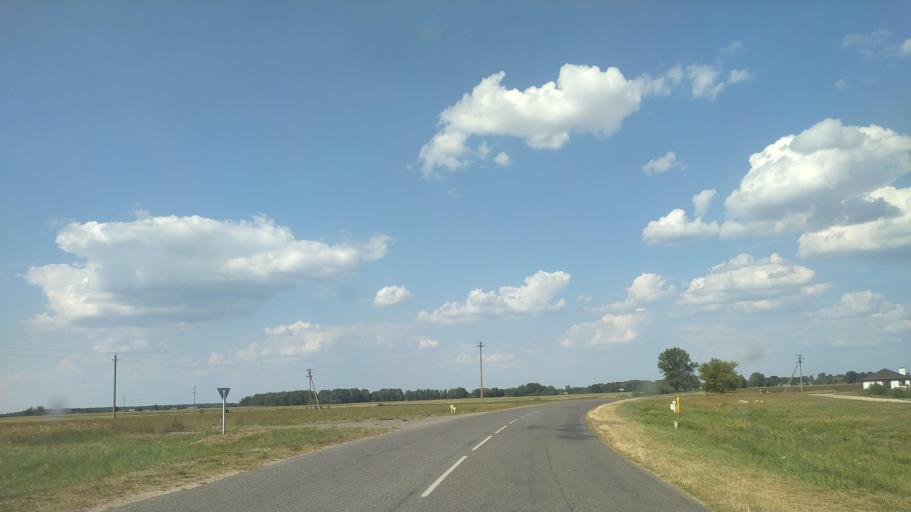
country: BY
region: Brest
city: Drahichyn
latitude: 52.1228
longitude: 25.1163
